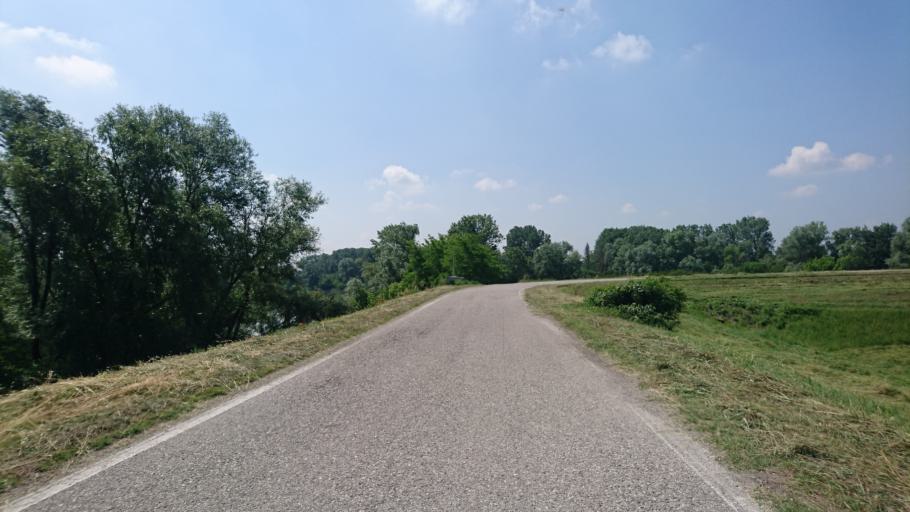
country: IT
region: Lombardy
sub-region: Provincia di Mantova
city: Sustinente
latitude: 45.0767
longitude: 10.9767
